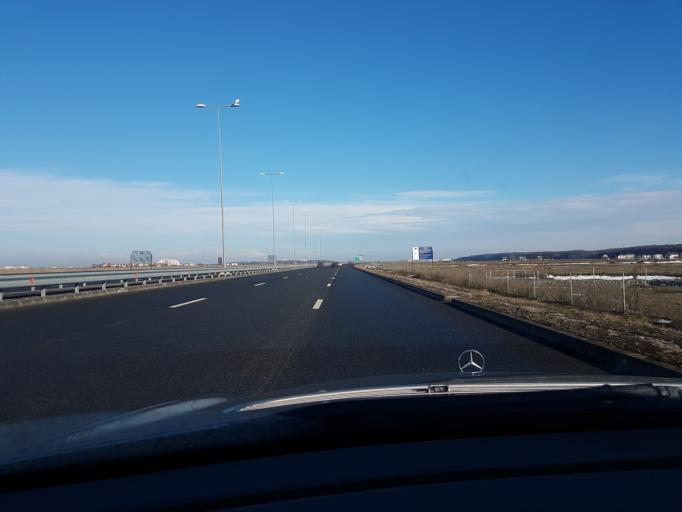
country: RO
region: Ilfov
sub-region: Voluntari City
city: Voluntari
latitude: 44.4987
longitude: 26.1533
